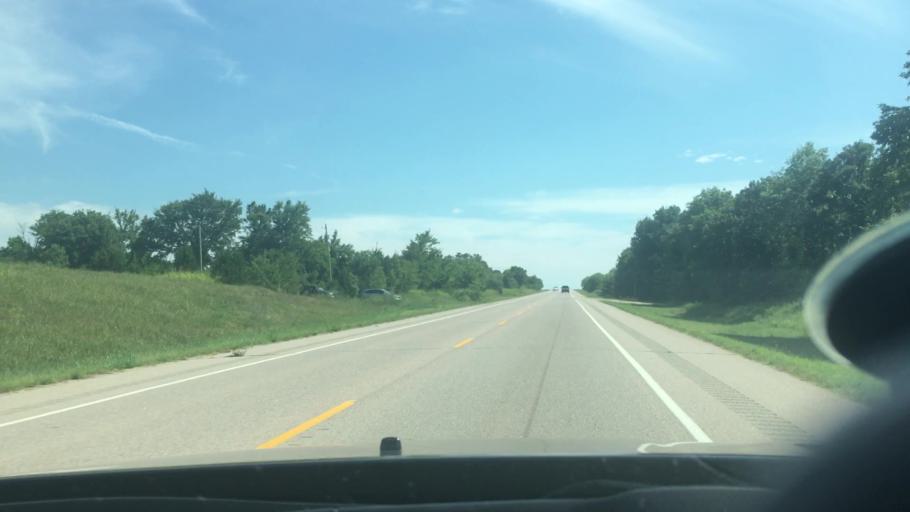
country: US
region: Oklahoma
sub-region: Seminole County
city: Konawa
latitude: 35.0055
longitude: -96.6788
